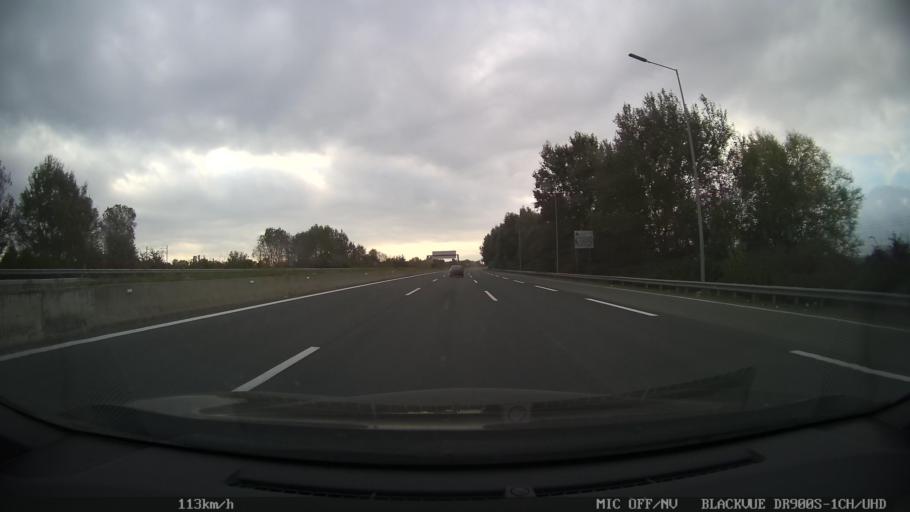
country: GR
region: Central Macedonia
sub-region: Nomos Pierias
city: Nea Efesos
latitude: 40.1877
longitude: 22.5506
